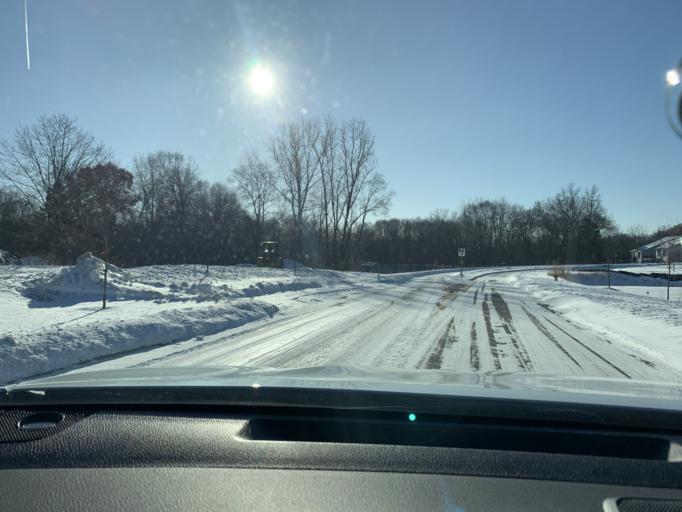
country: US
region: Minnesota
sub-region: Anoka County
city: Fridley
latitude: 45.0955
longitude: -93.2582
